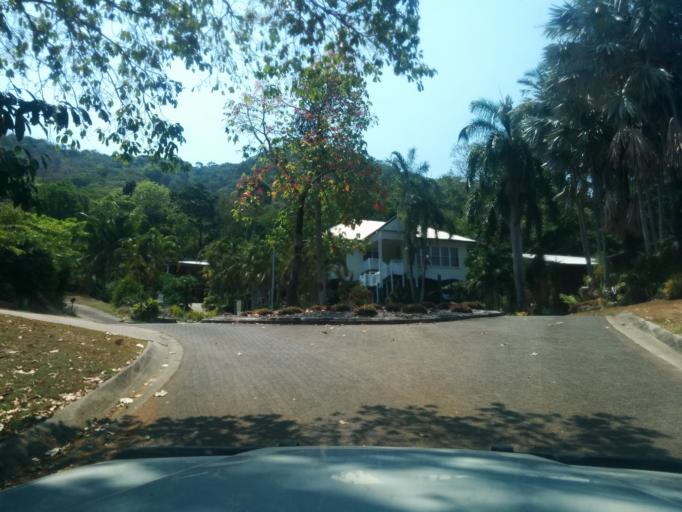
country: AU
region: Queensland
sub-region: Cairns
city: Cairns
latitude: -16.8853
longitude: 145.7445
